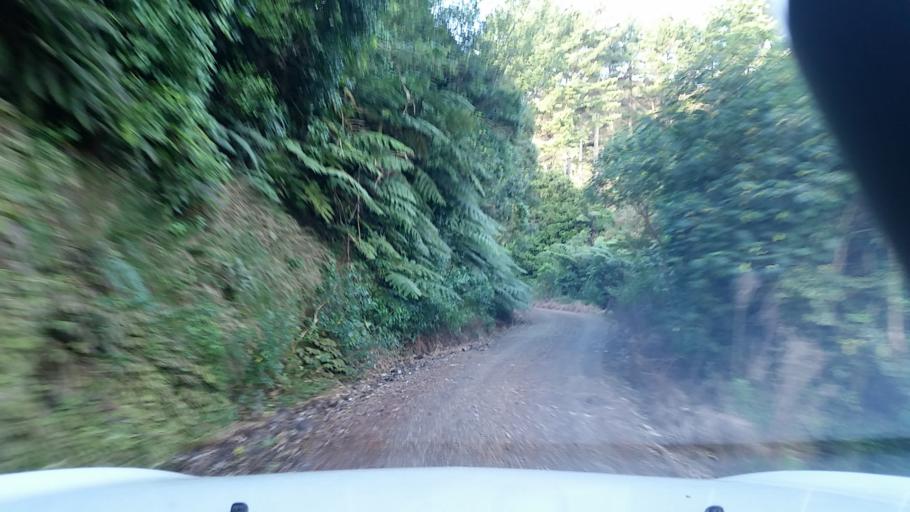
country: NZ
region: Taranaki
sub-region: New Plymouth District
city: Waitara
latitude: -38.9080
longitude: 174.5093
